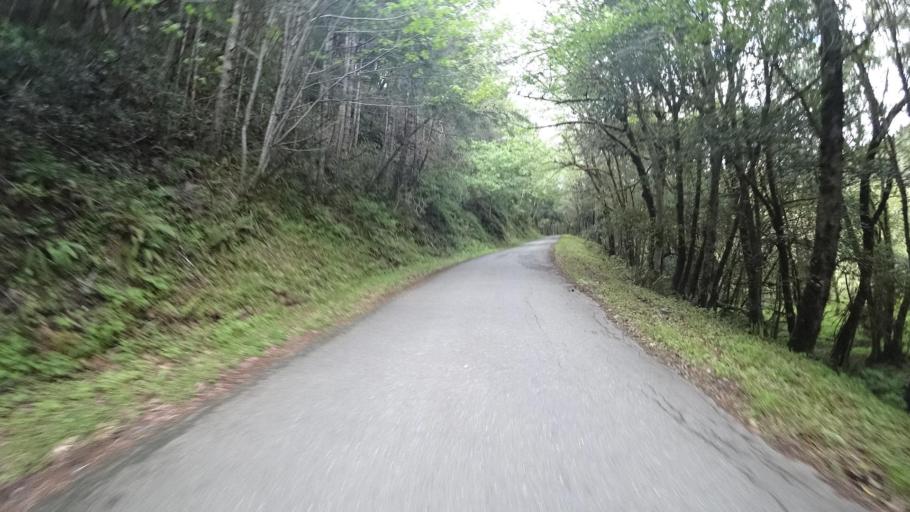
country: US
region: California
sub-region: Humboldt County
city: Blue Lake
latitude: 40.7661
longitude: -123.8910
